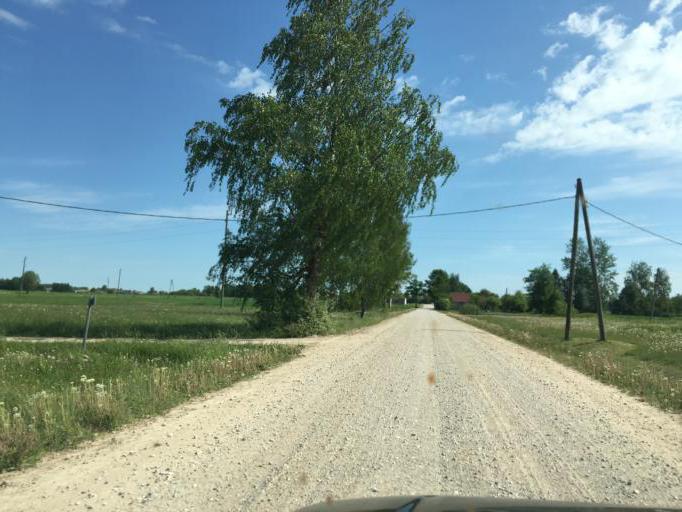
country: LV
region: Talsu Rajons
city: Valdemarpils
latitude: 57.3386
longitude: 22.4825
